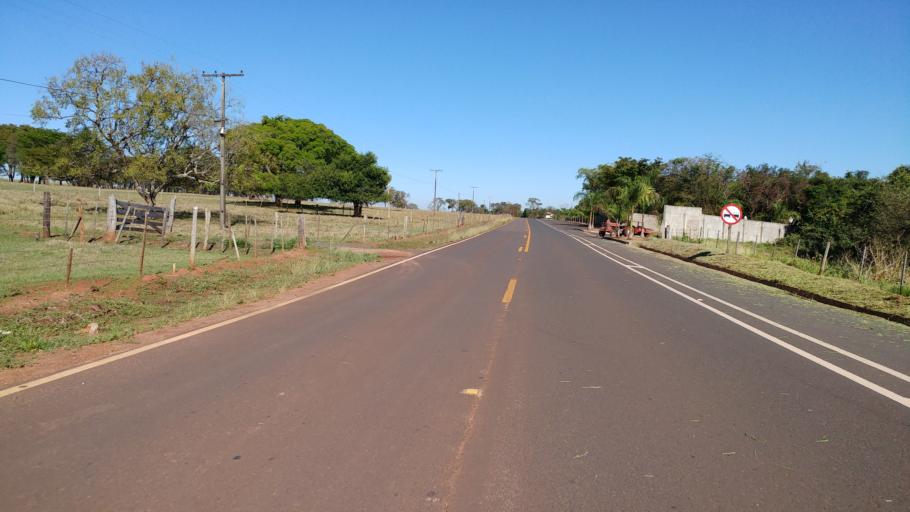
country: BR
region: Sao Paulo
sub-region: Paraguacu Paulista
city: Paraguacu Paulista
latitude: -22.4196
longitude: -50.6004
